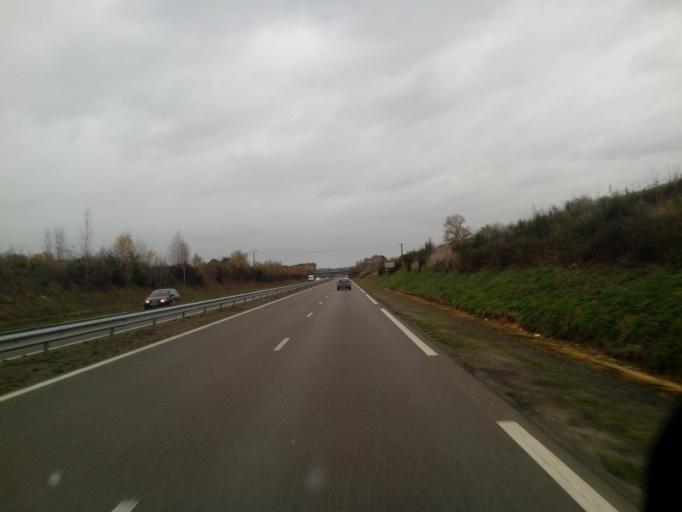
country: FR
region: Brittany
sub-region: Departement d'Ille-et-Vilaine
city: Betton
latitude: 48.1739
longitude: -1.6255
